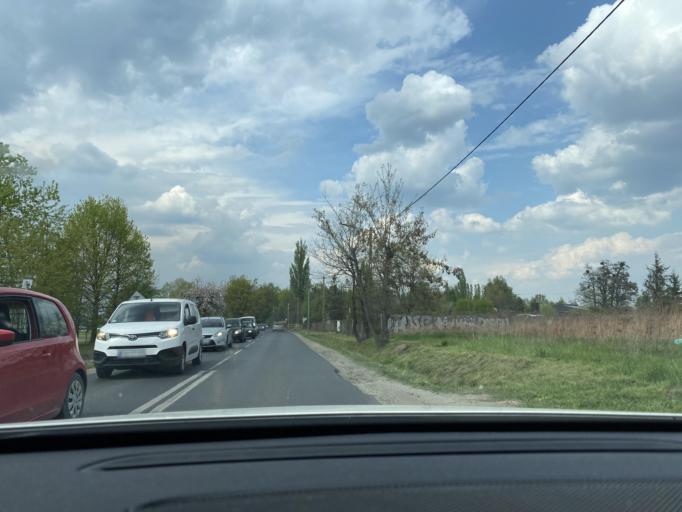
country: PL
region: Lower Silesian Voivodeship
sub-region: Powiat wroclawski
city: Wilczyce
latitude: 51.1222
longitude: 17.1203
